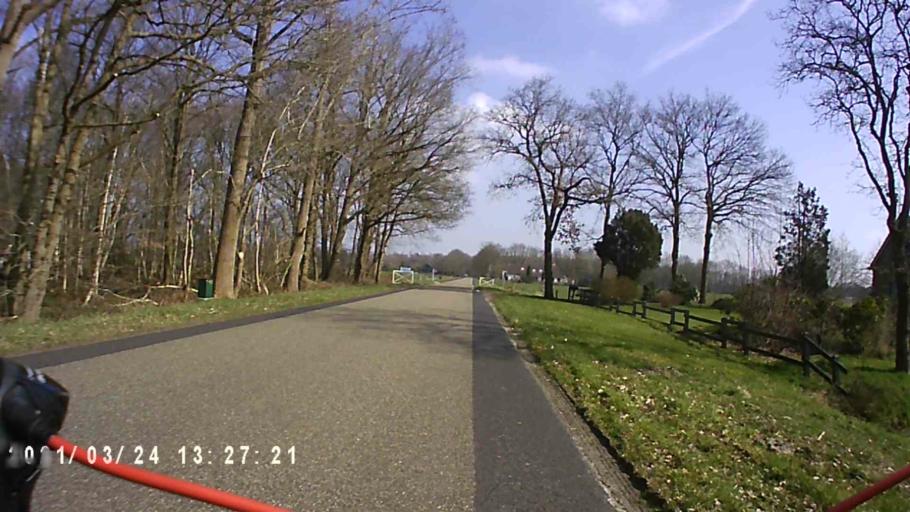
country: NL
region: Groningen
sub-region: Gemeente Leek
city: Leek
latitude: 53.0921
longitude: 6.2842
